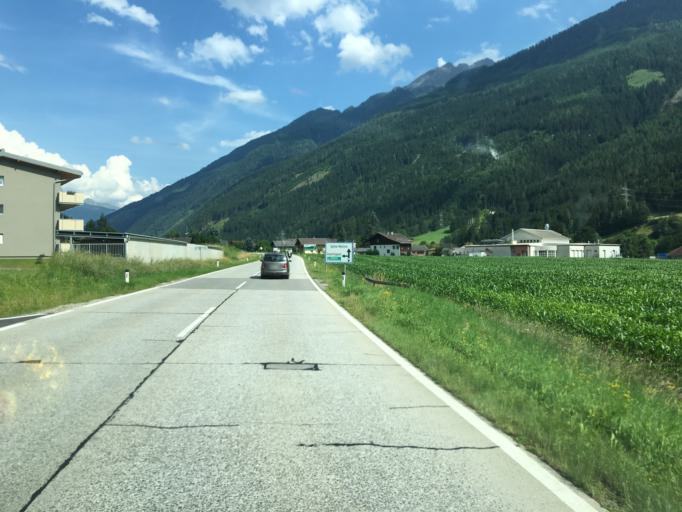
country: AT
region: Carinthia
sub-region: Politischer Bezirk Spittal an der Drau
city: Flattach
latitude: 46.9352
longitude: 13.1013
